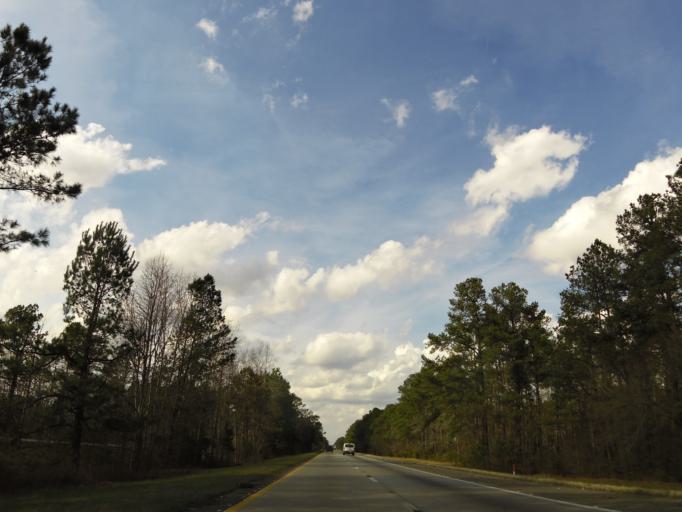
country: US
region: South Carolina
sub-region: Orangeburg County
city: Holly Hill
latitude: 33.2013
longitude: -80.4010
